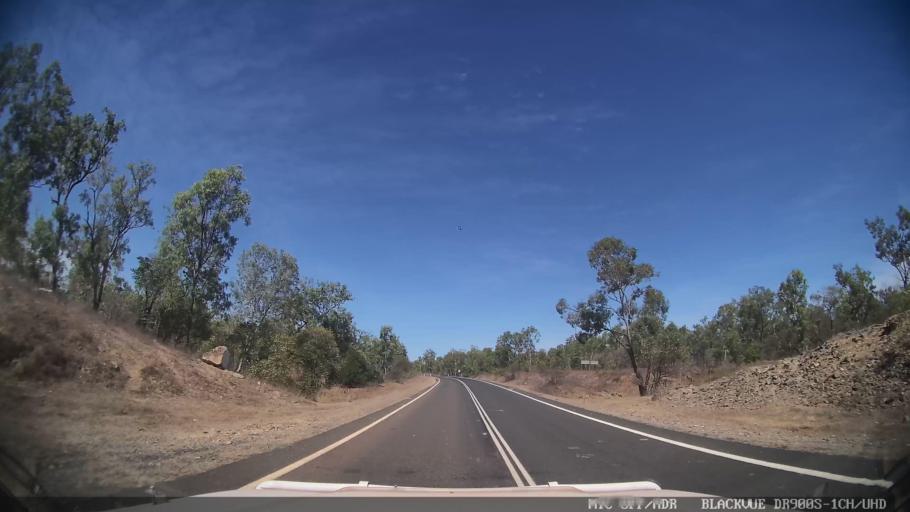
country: AU
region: Queensland
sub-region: Cook
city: Cooktown
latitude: -15.7112
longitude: 144.6147
